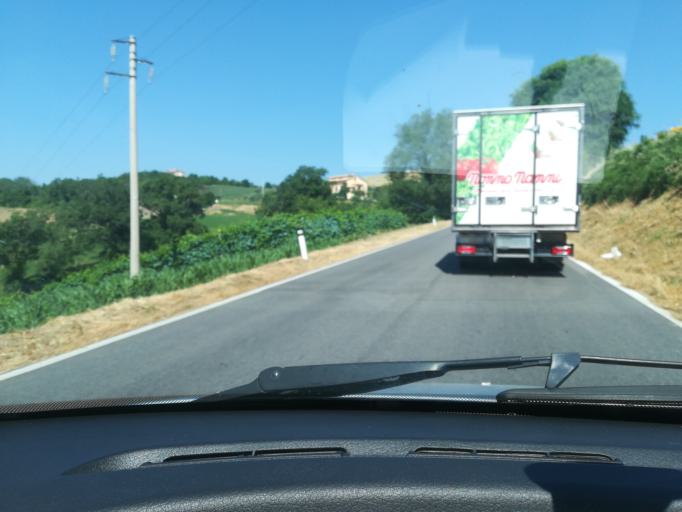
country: IT
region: The Marches
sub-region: Provincia di Macerata
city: Ripe San Ginesio
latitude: 43.1089
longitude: 13.3576
